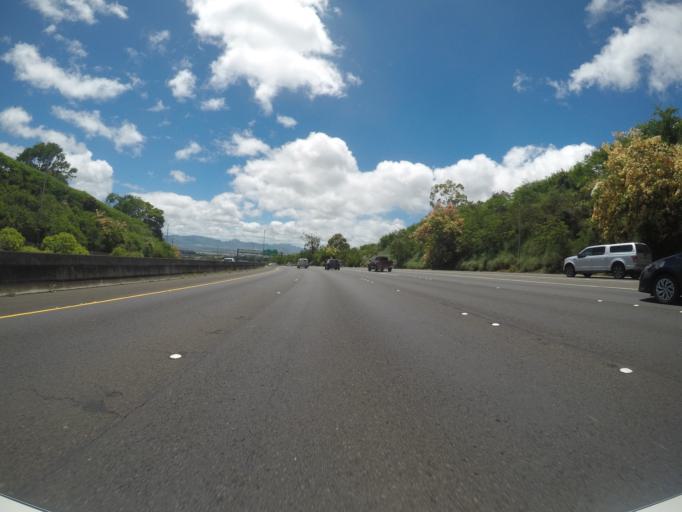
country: US
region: Hawaii
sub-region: Honolulu County
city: Halawa Heights
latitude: 21.3678
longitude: -157.9056
